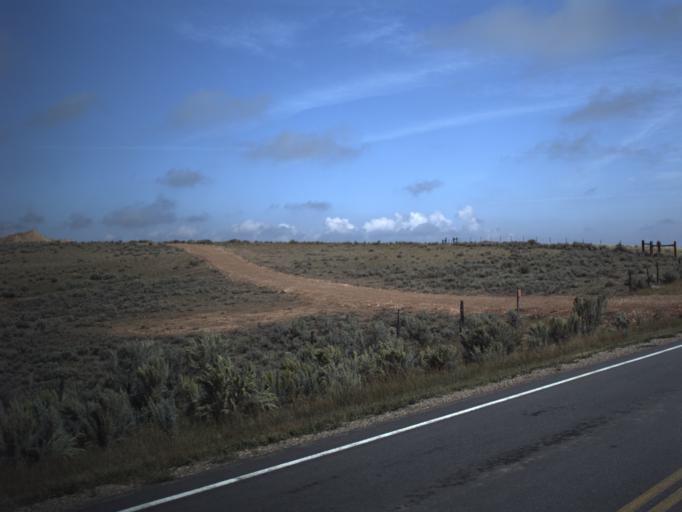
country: US
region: Utah
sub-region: Rich County
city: Randolph
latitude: 41.7628
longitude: -111.1302
